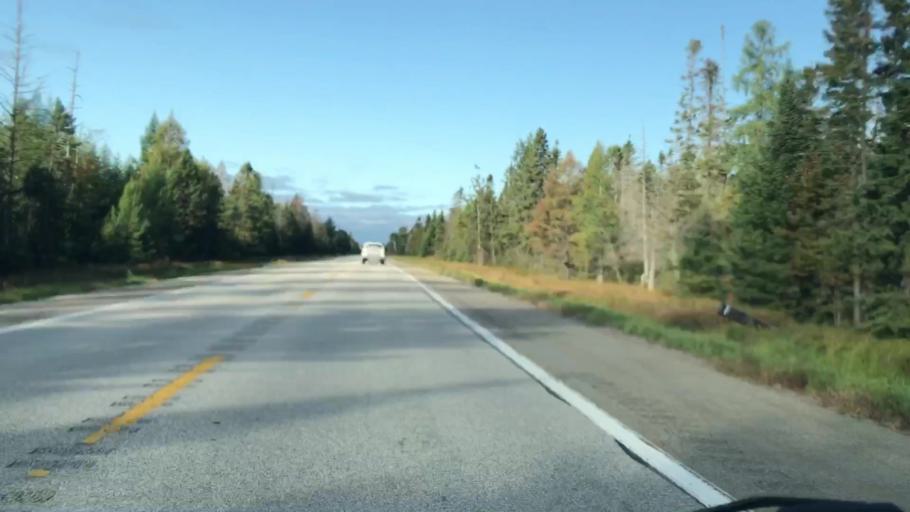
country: US
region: Michigan
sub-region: Luce County
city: Newberry
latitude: 46.3256
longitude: -85.1687
